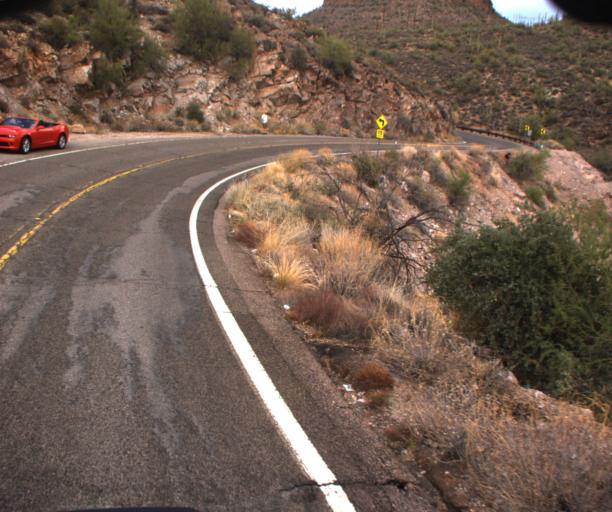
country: US
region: Arizona
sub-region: Pinal County
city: Apache Junction
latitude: 33.5426
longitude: -111.4440
